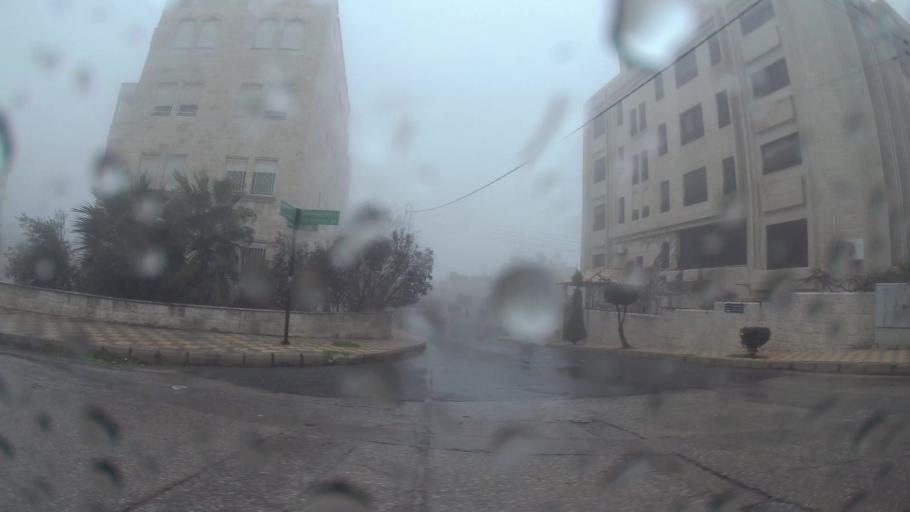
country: JO
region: Amman
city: Al Jubayhah
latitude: 32.0066
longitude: 35.8878
